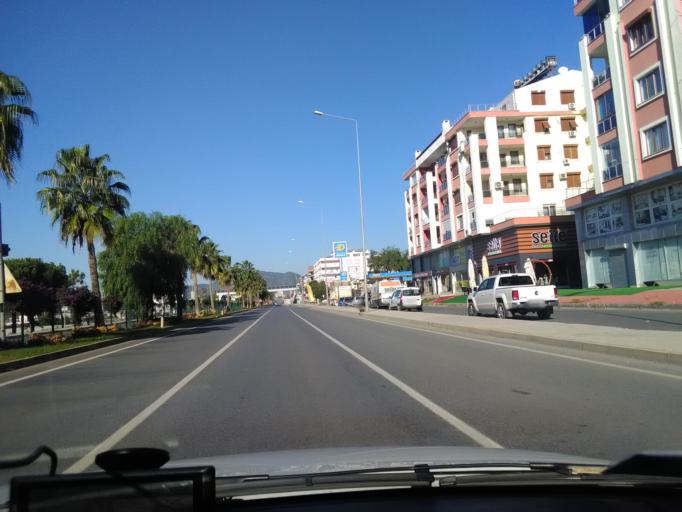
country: TR
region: Antalya
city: Gazipasa
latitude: 36.2742
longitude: 32.3089
